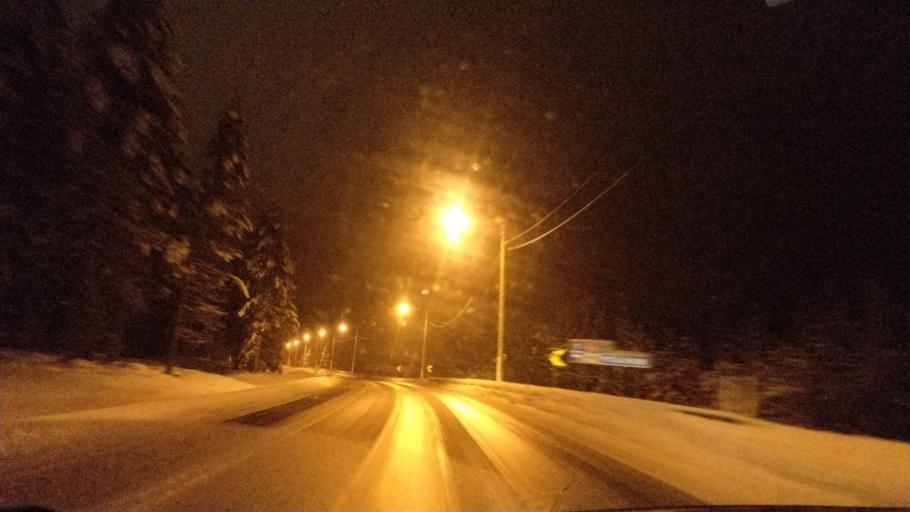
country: FI
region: Lapland
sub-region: Rovaniemi
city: Rovaniemi
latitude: 66.2739
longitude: 25.3295
